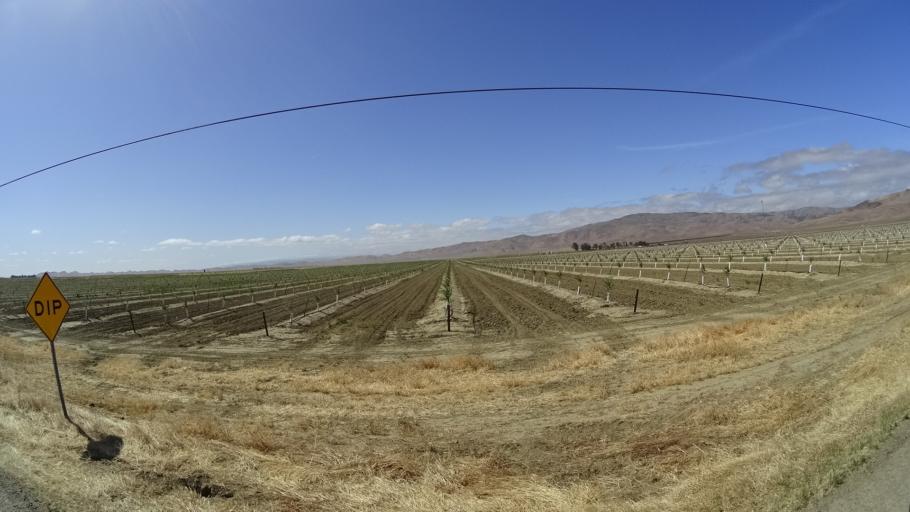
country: US
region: California
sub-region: Kings County
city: Avenal
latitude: 35.8179
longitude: -120.0844
